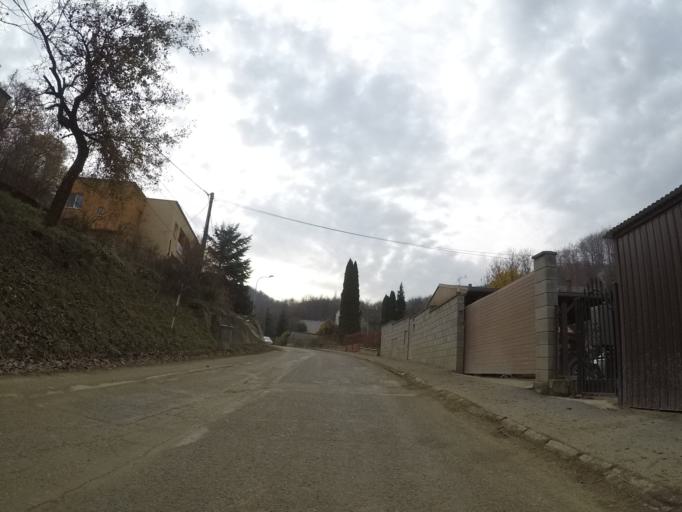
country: SK
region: Presovsky
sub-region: Okres Presov
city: Presov
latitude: 48.9826
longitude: 21.2171
